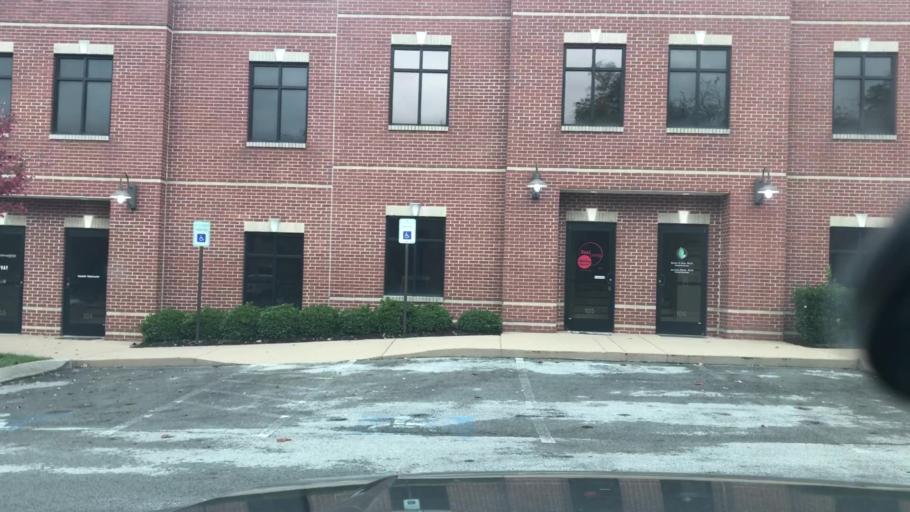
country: US
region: Tennessee
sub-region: Williamson County
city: Franklin
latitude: 35.9390
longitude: -86.8322
